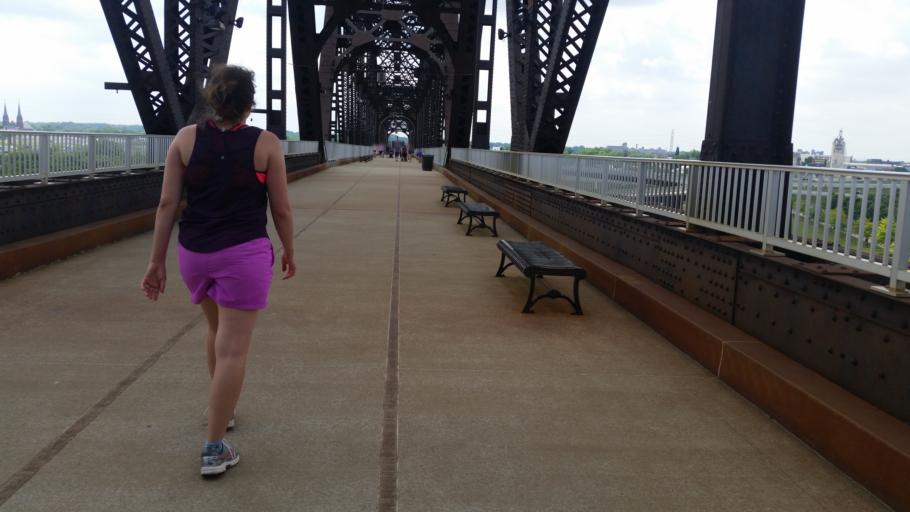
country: US
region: Indiana
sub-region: Clark County
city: Jeffersonville
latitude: 38.2643
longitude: -85.7384
